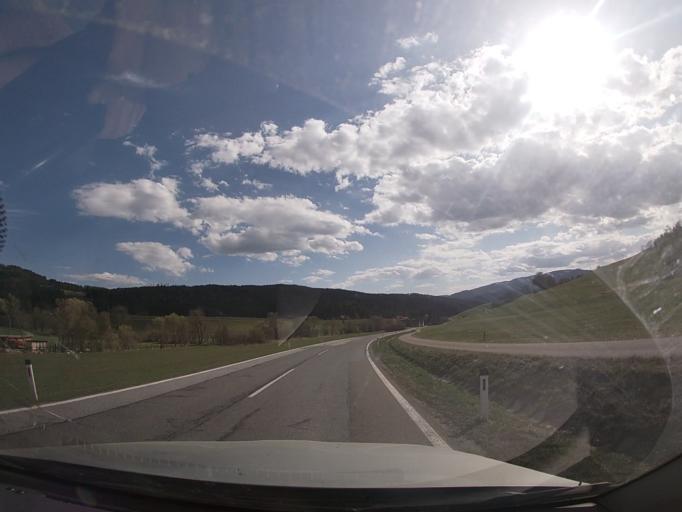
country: AT
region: Styria
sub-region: Politischer Bezirk Murau
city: Perchau am Sattel
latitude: 47.1023
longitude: 14.4558
